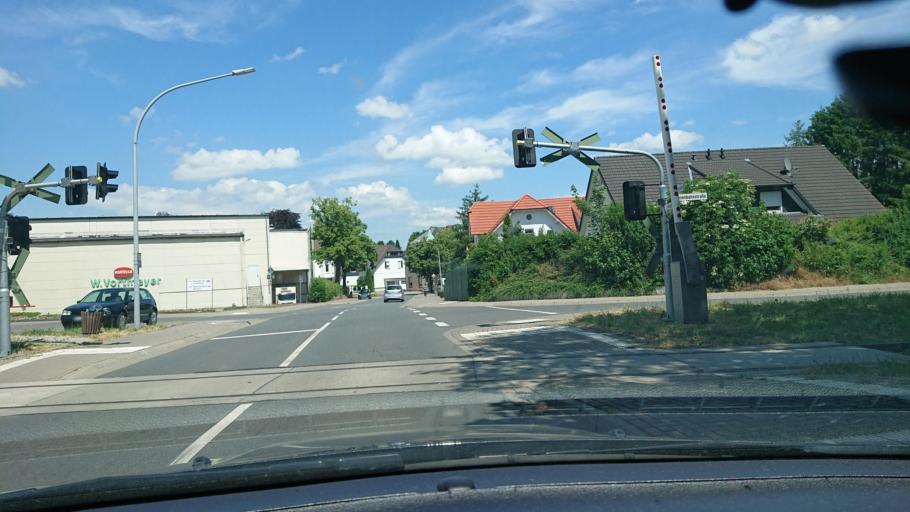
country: DE
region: North Rhine-Westphalia
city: Preussisch Oldendorf
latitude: 52.3033
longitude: 8.4903
